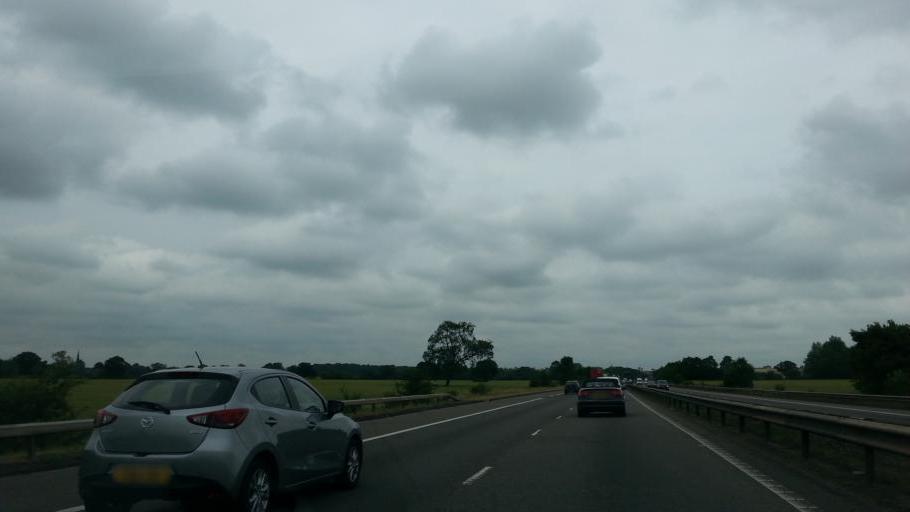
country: GB
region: England
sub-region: Derbyshire
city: Netherseal
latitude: 52.6529
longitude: -1.5880
